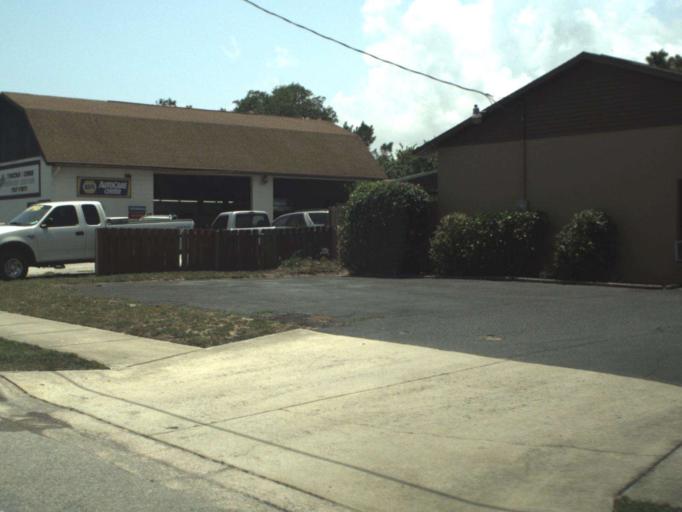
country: US
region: Florida
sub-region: Volusia County
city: Port Orange
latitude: 29.1173
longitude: -80.9749
